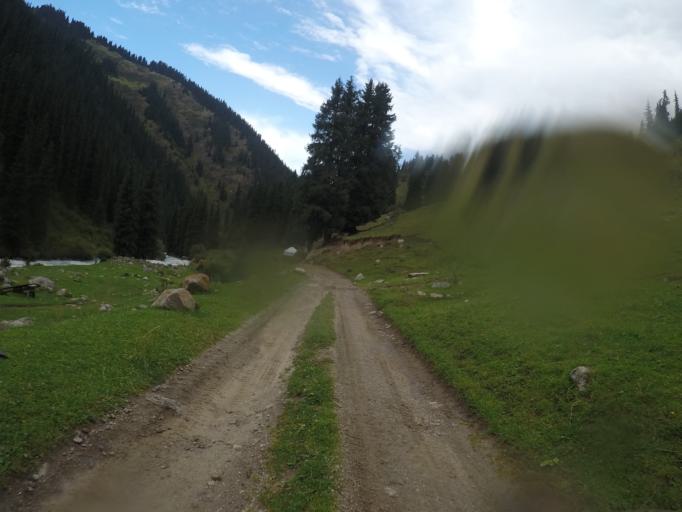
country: KG
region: Ysyk-Koel
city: Teploklyuchenka
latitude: 42.4122
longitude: 78.5751
